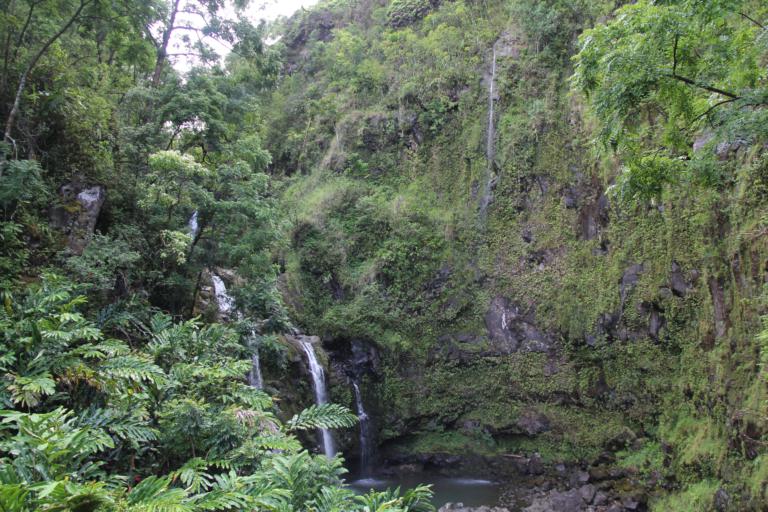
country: US
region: Hawaii
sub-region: Maui County
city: Wailua
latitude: 20.8325
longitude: -156.1387
